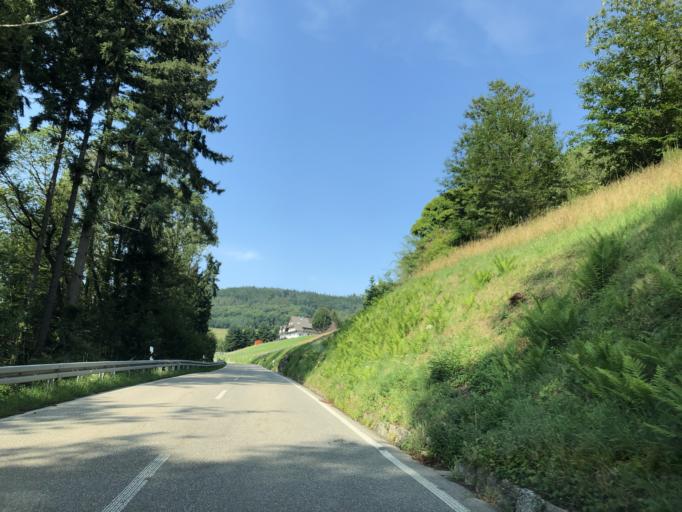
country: DE
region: Baden-Wuerttemberg
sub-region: Freiburg Region
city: Sasbachwalden
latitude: 48.6135
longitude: 8.1402
